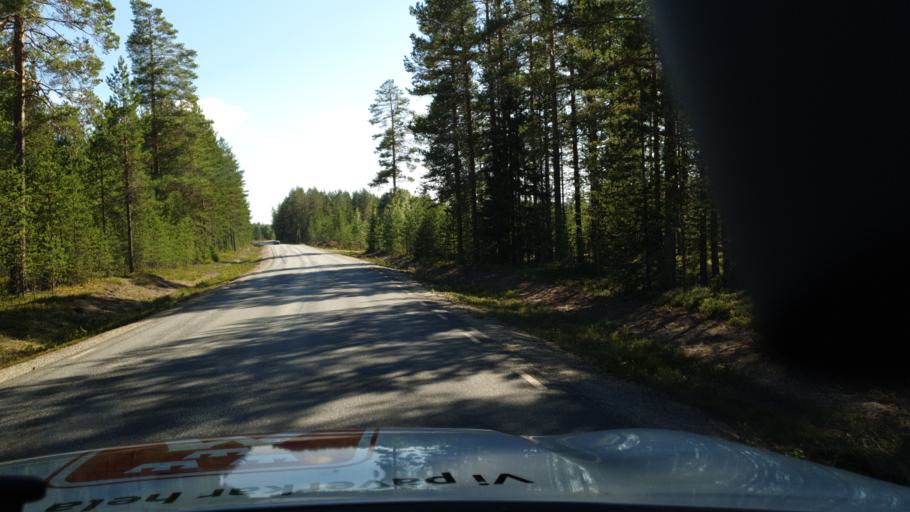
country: SE
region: Vaesterbotten
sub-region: Umea Kommun
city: Roback
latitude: 63.9784
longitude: 20.1176
